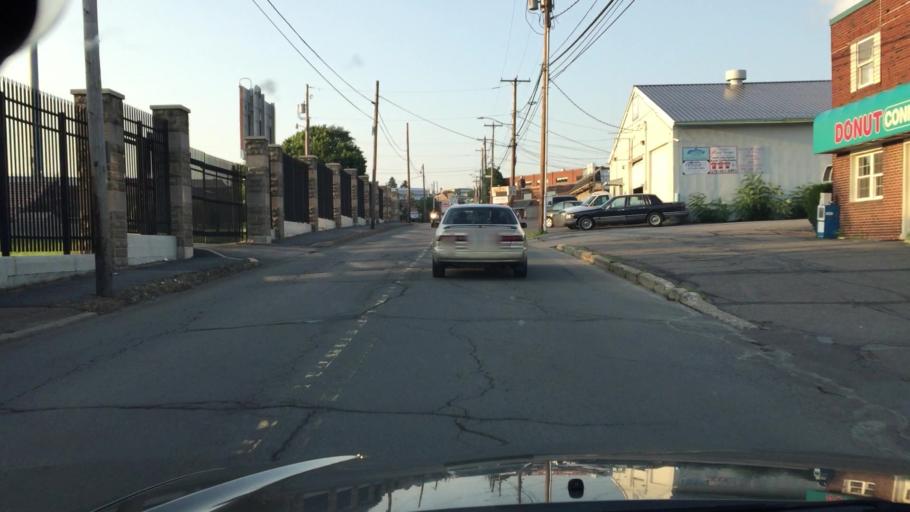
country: US
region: Pennsylvania
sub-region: Luzerne County
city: Hazleton
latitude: 40.9573
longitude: -75.9691
